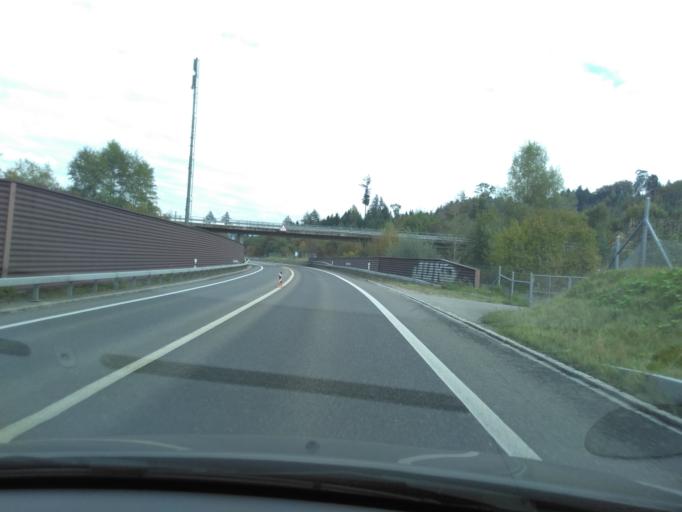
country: CH
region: Saint Gallen
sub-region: Wahlkreis See-Gaster
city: Eschenbach
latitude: 47.2282
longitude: 8.8908
